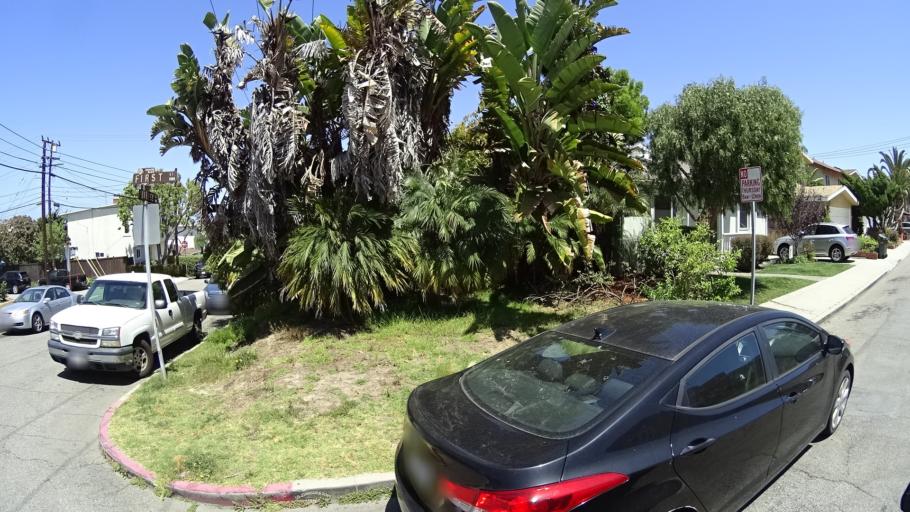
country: US
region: California
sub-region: Los Angeles County
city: Redondo Beach
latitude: 33.8562
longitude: -118.3872
